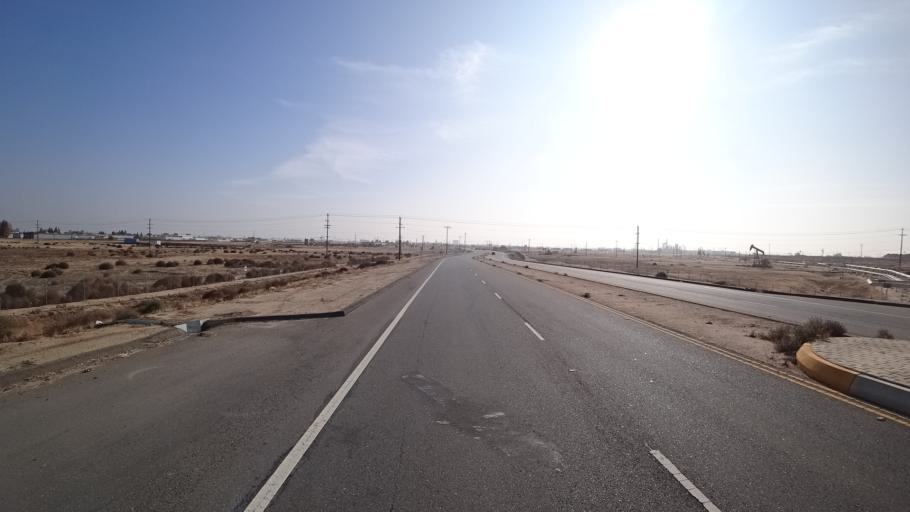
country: US
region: California
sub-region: Kern County
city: Greenacres
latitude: 35.3913
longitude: -119.0657
